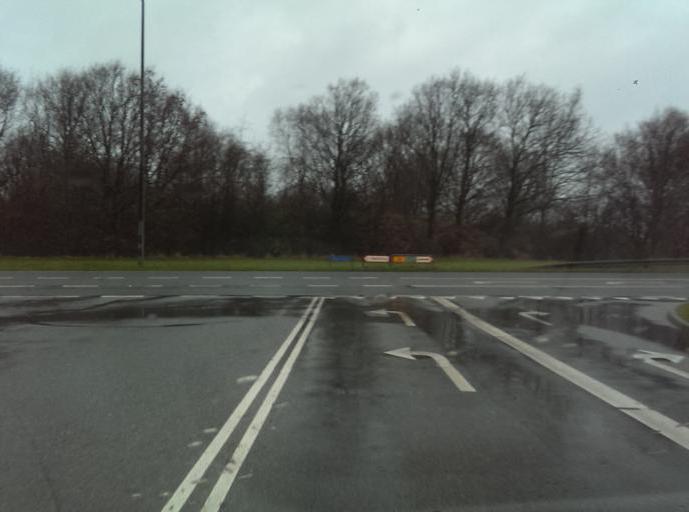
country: DK
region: South Denmark
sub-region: Esbjerg Kommune
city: Esbjerg
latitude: 55.5083
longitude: 8.4401
